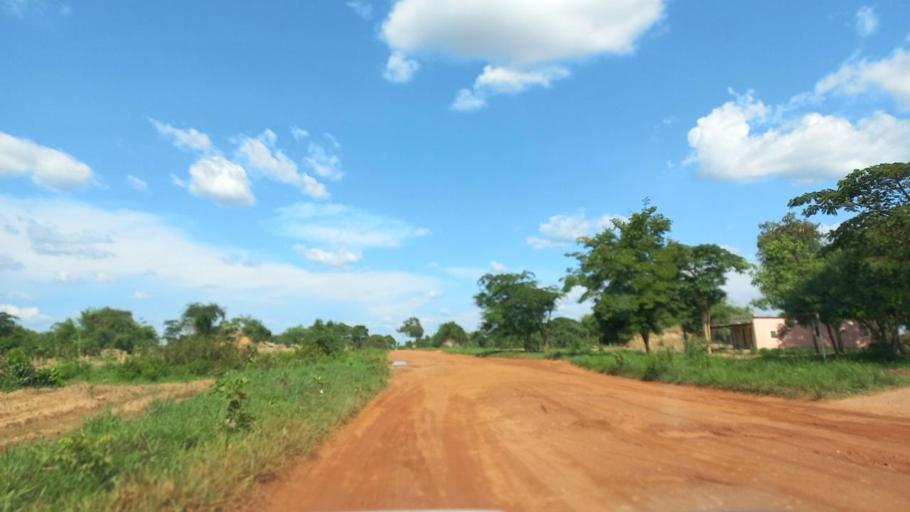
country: ZM
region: Copperbelt
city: Kitwe
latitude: -12.8675
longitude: 28.3668
